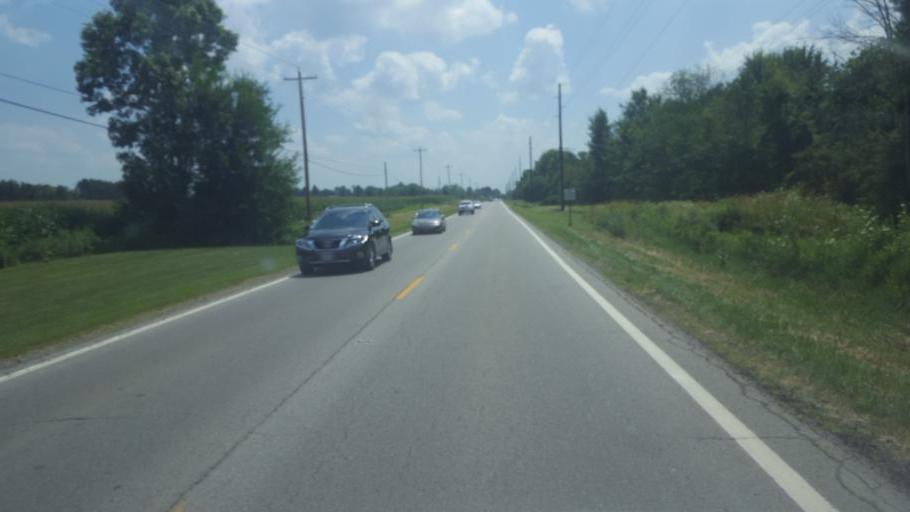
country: US
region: Ohio
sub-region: Crawford County
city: Crestline
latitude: 40.7531
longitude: -82.7459
